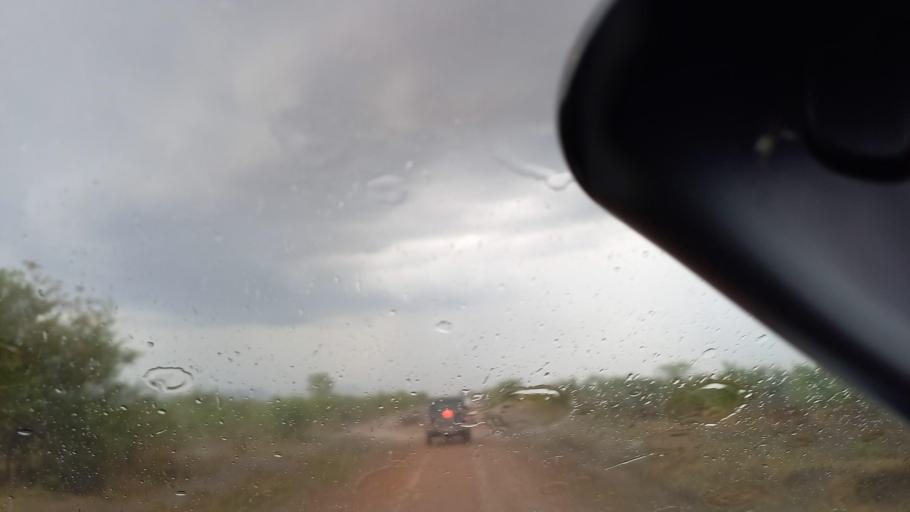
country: ZM
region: Lusaka
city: Kafue
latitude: -15.8645
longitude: 28.1746
